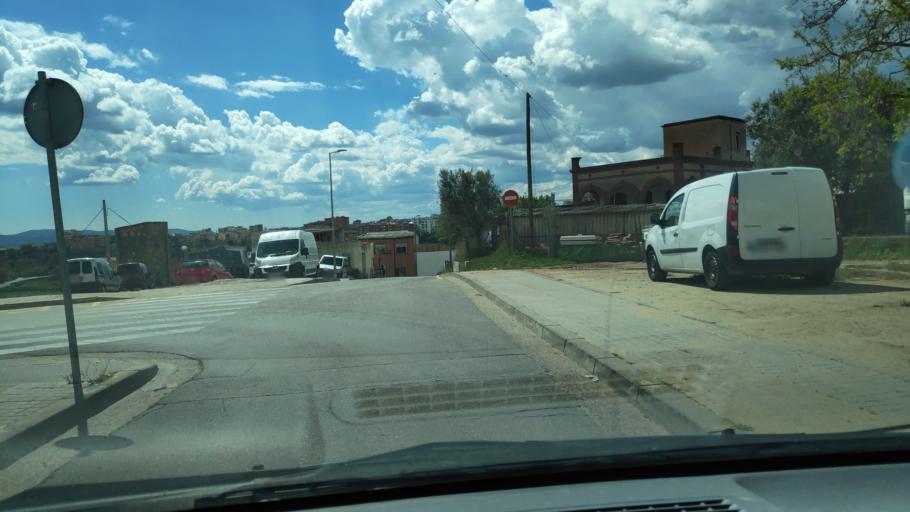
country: ES
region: Catalonia
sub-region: Provincia de Barcelona
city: Sabadell
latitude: 41.5508
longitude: 2.1252
